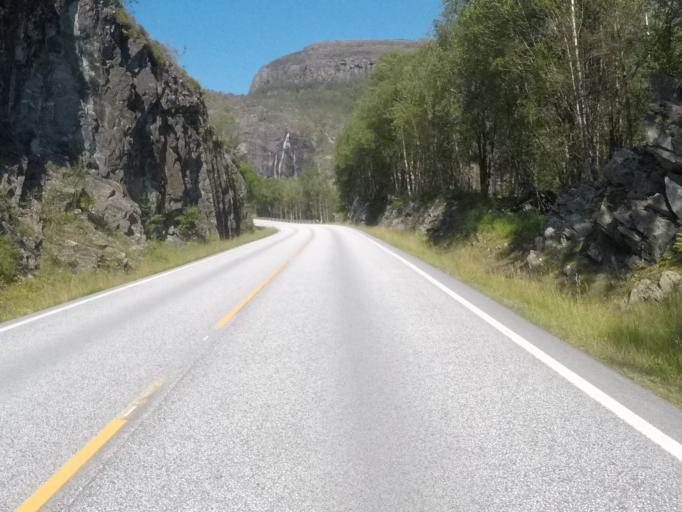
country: NO
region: Sogn og Fjordane
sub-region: Bremanger
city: Svelgen
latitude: 61.6404
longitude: 5.2961
